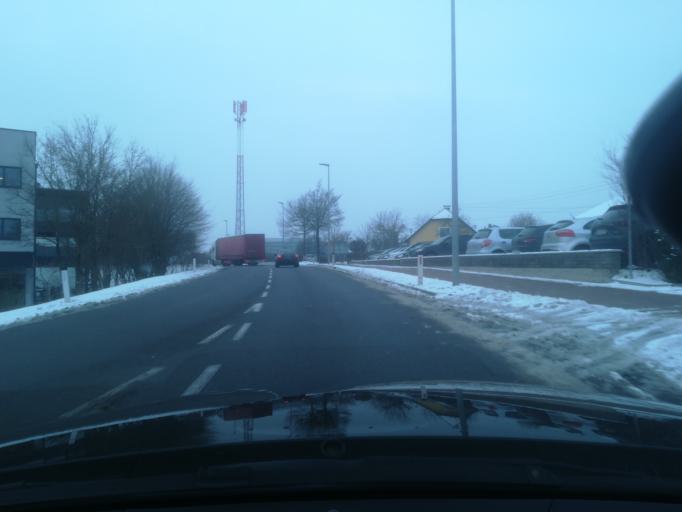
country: AT
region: Upper Austria
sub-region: Wels-Land
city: Marchtrenk
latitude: 48.1903
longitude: 14.1055
